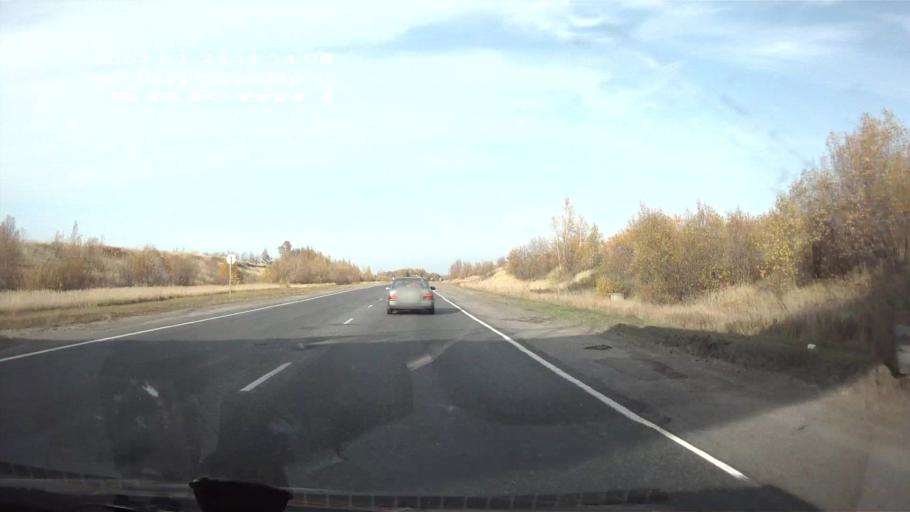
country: RU
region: Chuvashia
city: Kugesi
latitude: 56.0417
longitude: 47.3662
